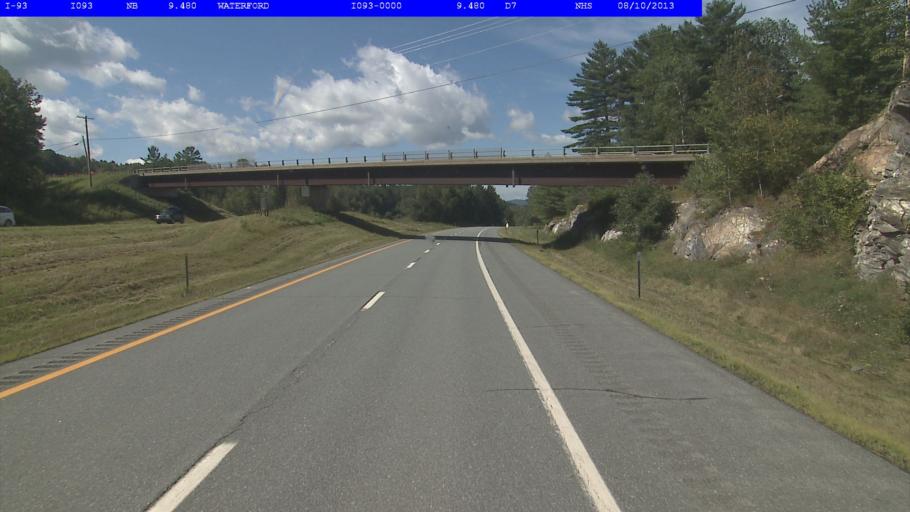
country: US
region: Vermont
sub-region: Caledonia County
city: Saint Johnsbury
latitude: 44.4115
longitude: -71.9885
